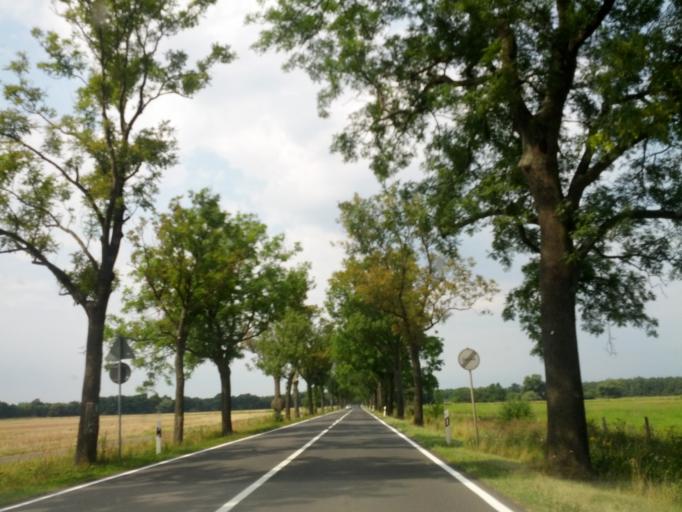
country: DE
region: Brandenburg
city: Nauen
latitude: 52.6495
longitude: 12.9261
